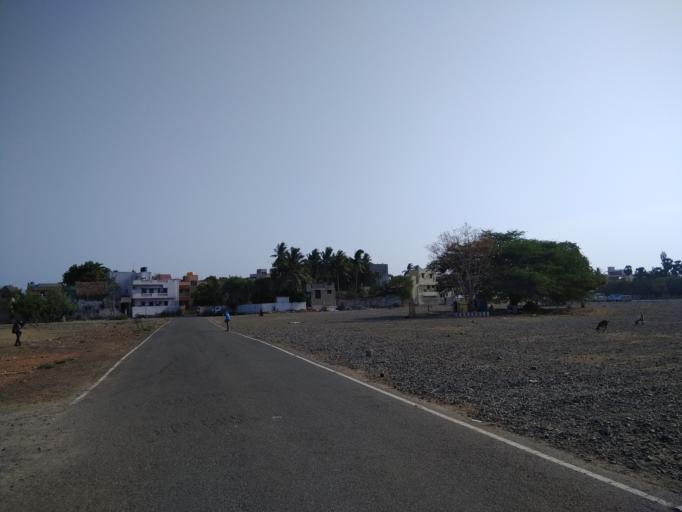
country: IN
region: Tamil Nadu
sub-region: Kancheepuram
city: Saint Thomas Mount
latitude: 13.0134
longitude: 80.1881
